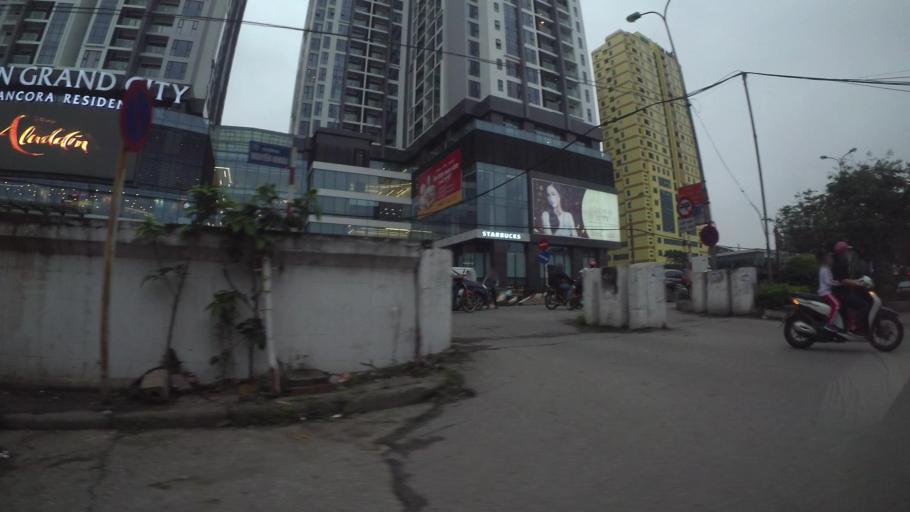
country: VN
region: Ha Noi
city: Hai BaTrung
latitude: 21.0114
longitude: 105.8642
